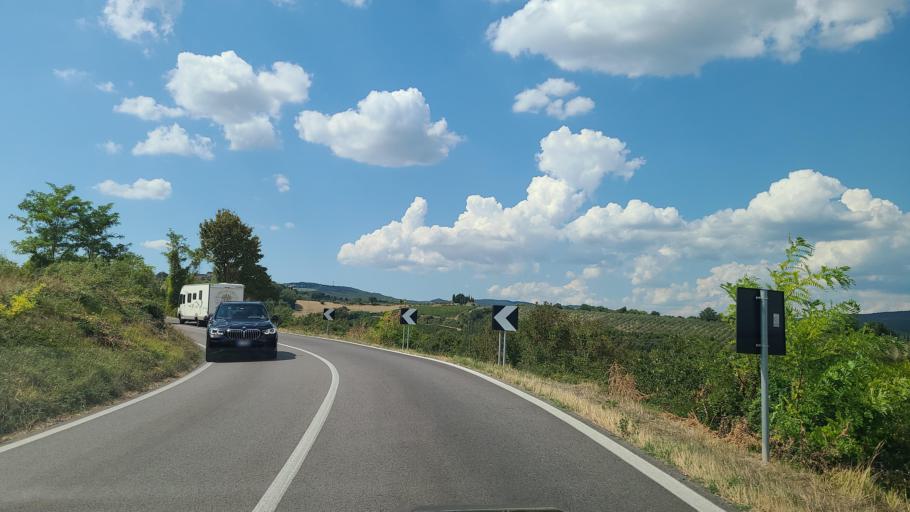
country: IT
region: Tuscany
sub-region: Provincia di Siena
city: Casole d'Elsa
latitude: 43.4032
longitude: 11.0343
